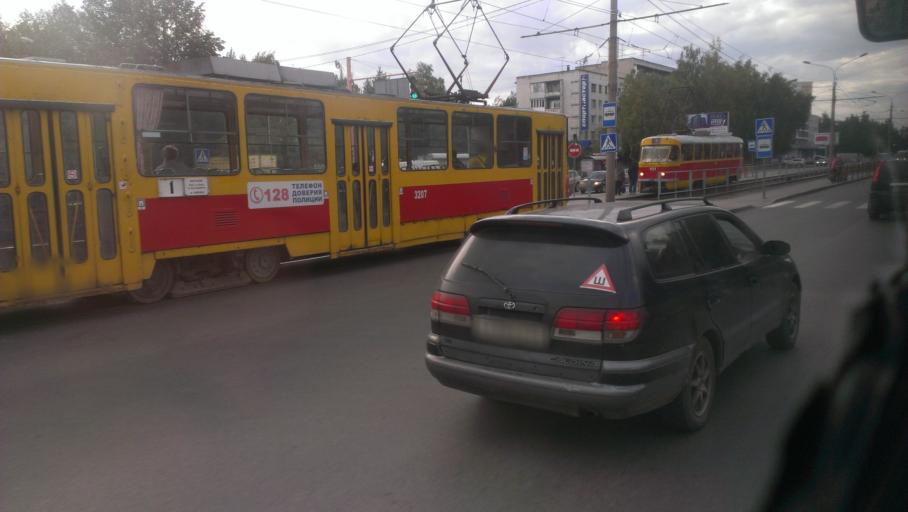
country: RU
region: Altai Krai
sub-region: Gorod Barnaulskiy
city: Barnaul
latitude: 53.3447
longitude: 83.7664
